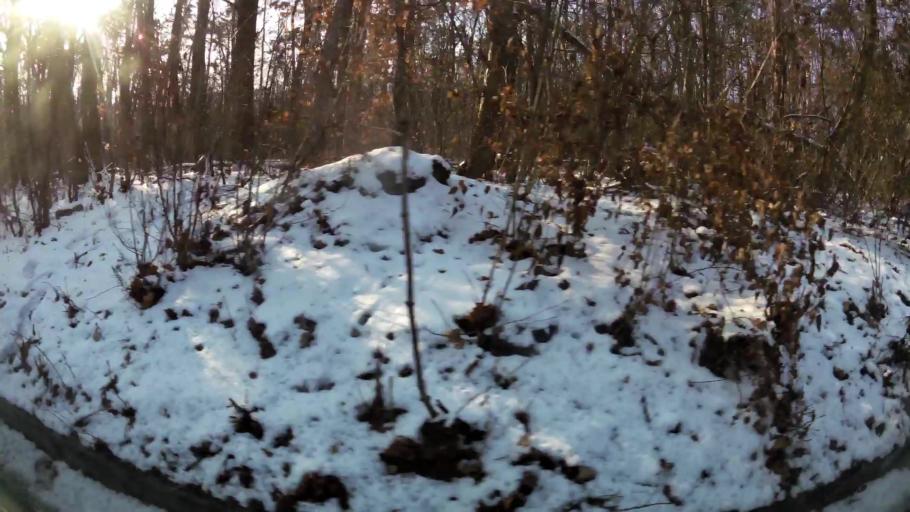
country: BG
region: Sofia-Capital
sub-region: Stolichna Obshtina
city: Sofia
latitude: 42.6698
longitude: 23.3439
